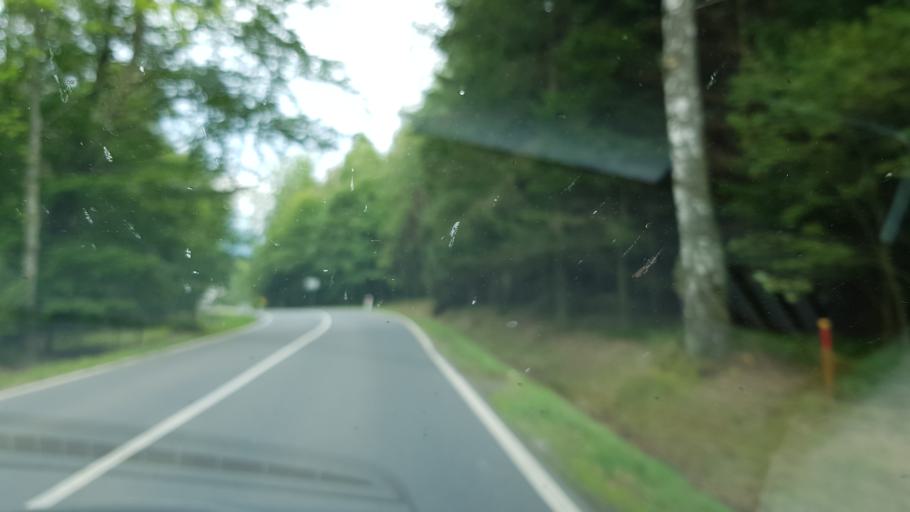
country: CZ
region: Pardubicky
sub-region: Okres Usti nad Orlici
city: Kraliky
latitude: 50.1023
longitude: 16.7850
